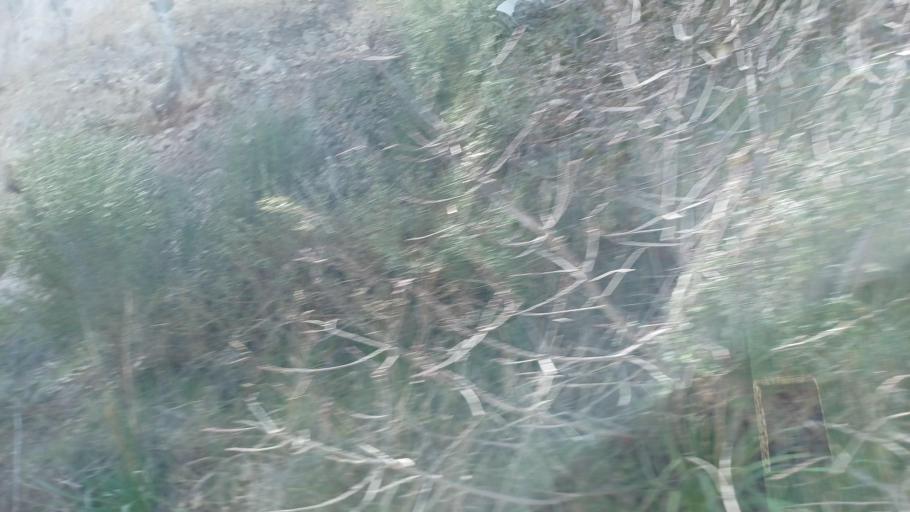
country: CY
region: Limassol
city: Pachna
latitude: 34.8041
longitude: 32.6901
